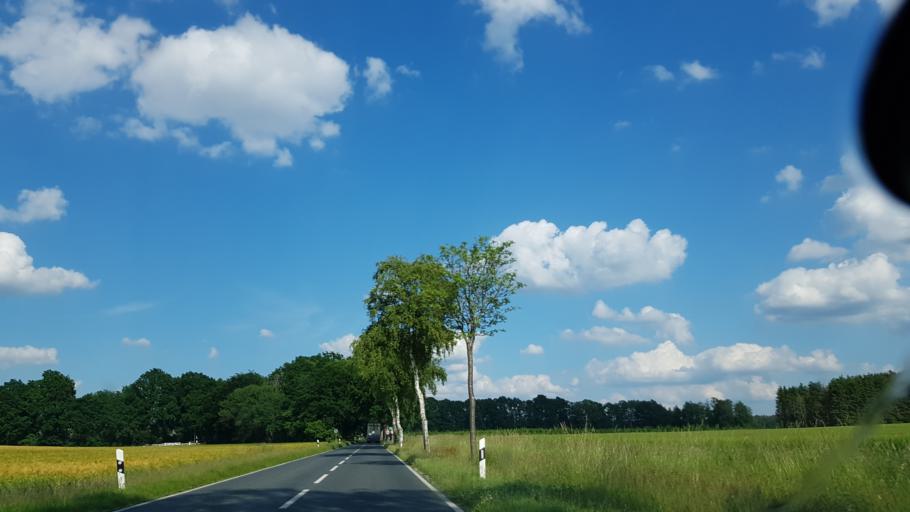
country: DE
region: Lower Saxony
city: Wenzendorf
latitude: 53.3470
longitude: 9.7908
